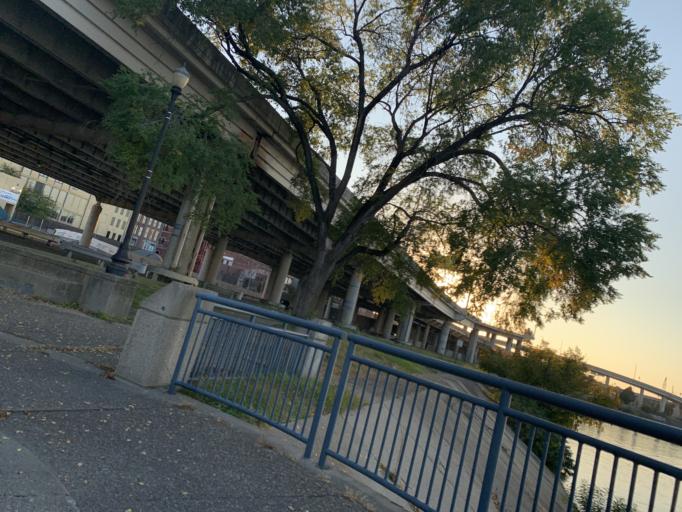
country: US
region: Kentucky
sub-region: Jefferson County
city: Louisville
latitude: 38.2590
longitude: -85.7615
